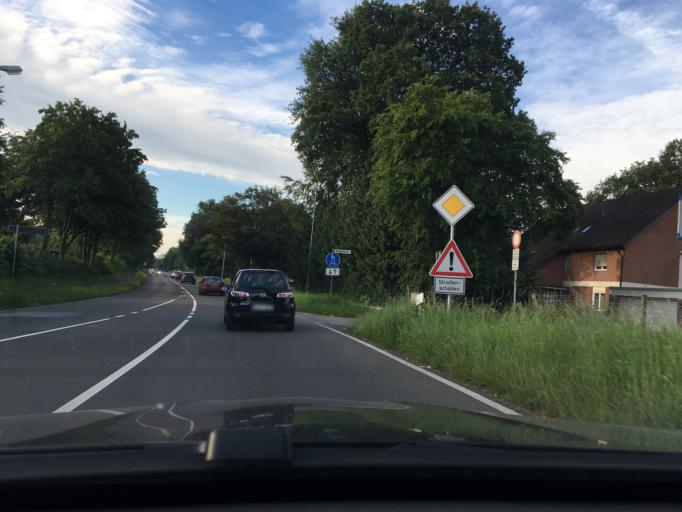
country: DE
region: North Rhine-Westphalia
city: Opladen
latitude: 51.0546
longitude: 7.0571
